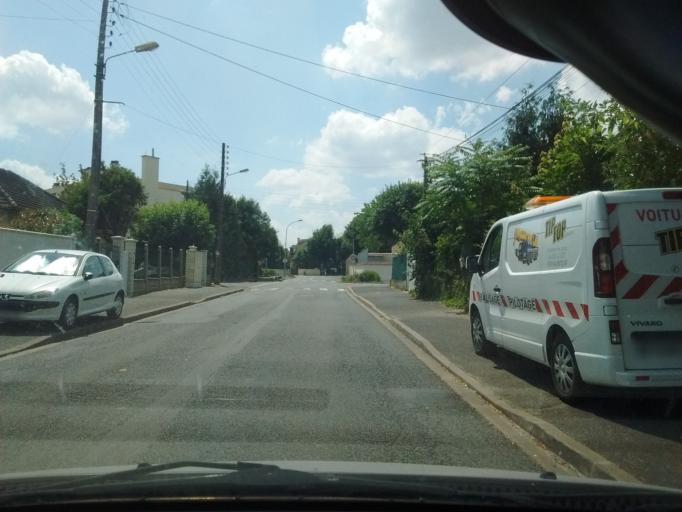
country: FR
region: Ile-de-France
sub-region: Departement de Seine-et-Marne
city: Ponthierry
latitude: 48.5328
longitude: 2.5351
